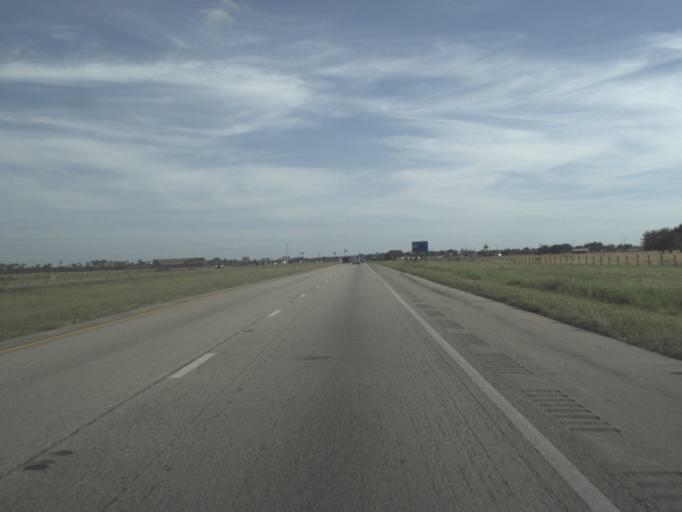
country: US
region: Florida
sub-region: Charlotte County
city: Punta Gorda
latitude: 26.9109
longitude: -82.0107
